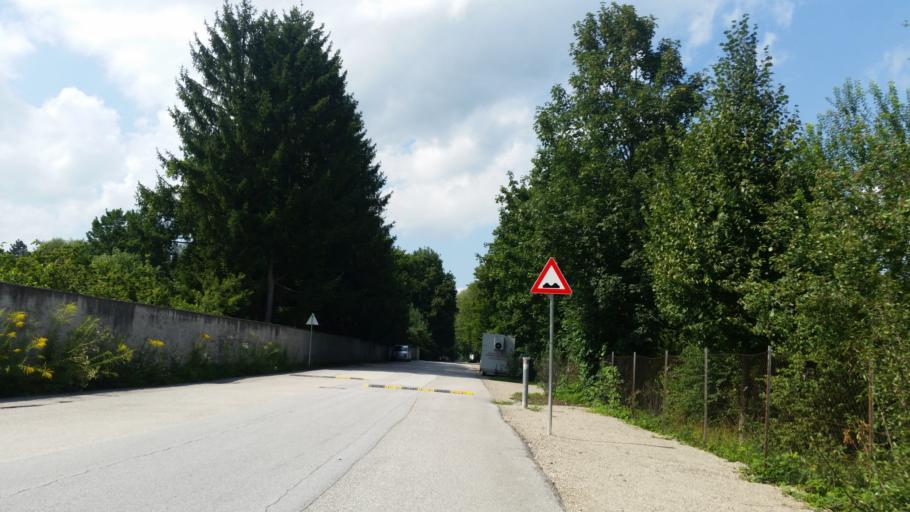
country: AT
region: Salzburg
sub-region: Politischer Bezirk Salzburg-Umgebung
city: Bergheim
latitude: 47.8375
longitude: 13.0149
